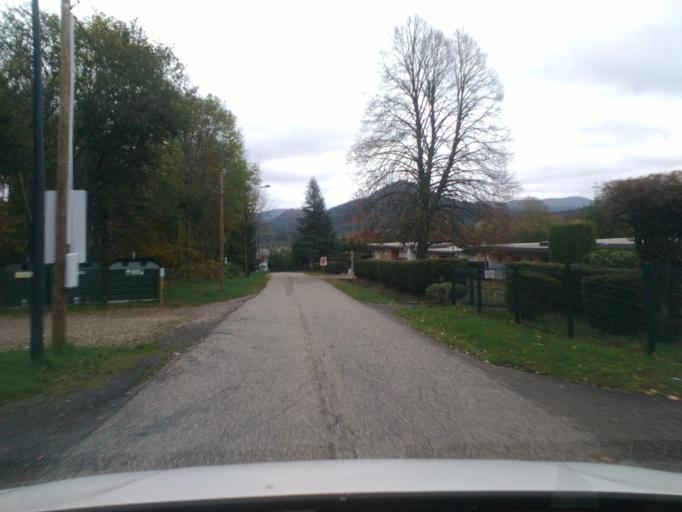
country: FR
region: Lorraine
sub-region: Departement des Vosges
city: Ban-de-Laveline
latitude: 48.3499
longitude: 7.0994
